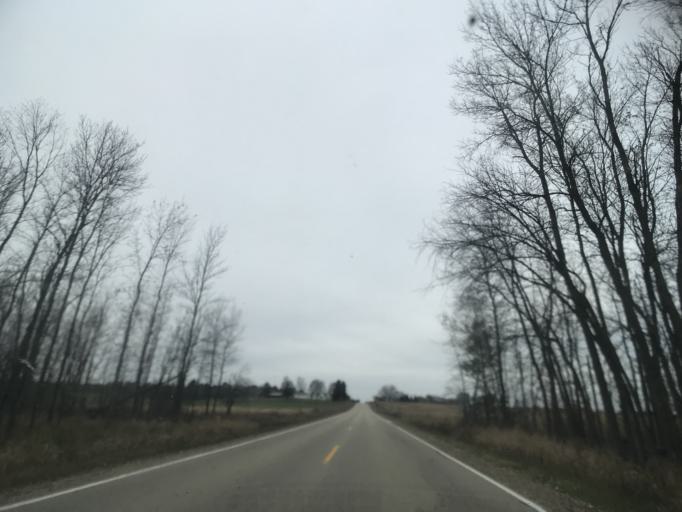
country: US
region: Wisconsin
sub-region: Oconto County
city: Gillett
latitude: 44.9835
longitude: -88.3073
